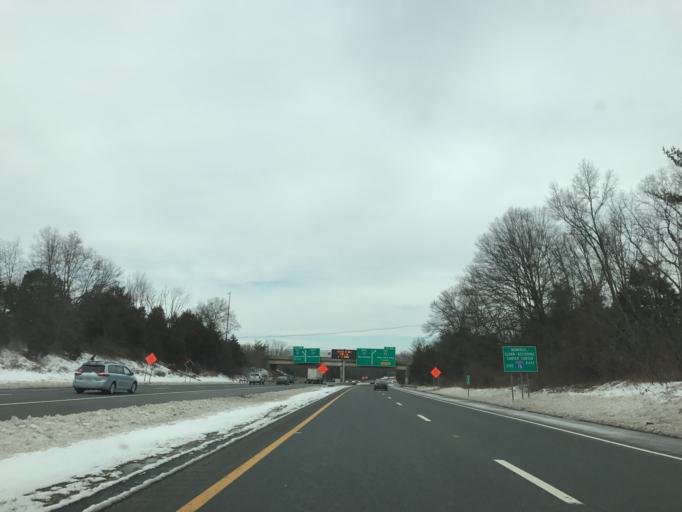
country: US
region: New Jersey
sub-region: Somerset County
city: Bridgewater
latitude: 40.6254
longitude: -74.6400
